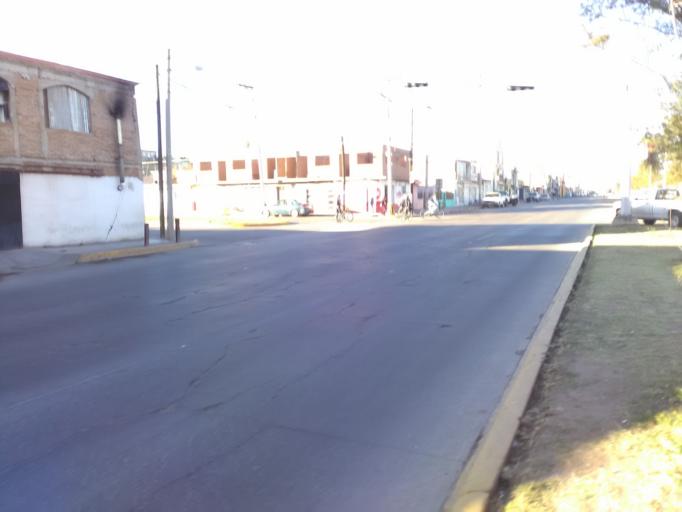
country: MX
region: Durango
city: Victoria de Durango
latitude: 24.0494
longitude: -104.6485
